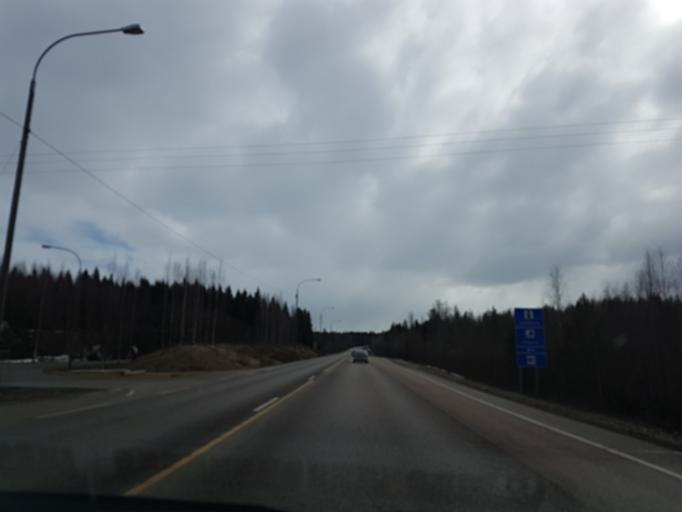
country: FI
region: Northern Savo
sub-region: Varkaus
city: Leppaevirta
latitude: 62.4433
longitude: 27.8002
